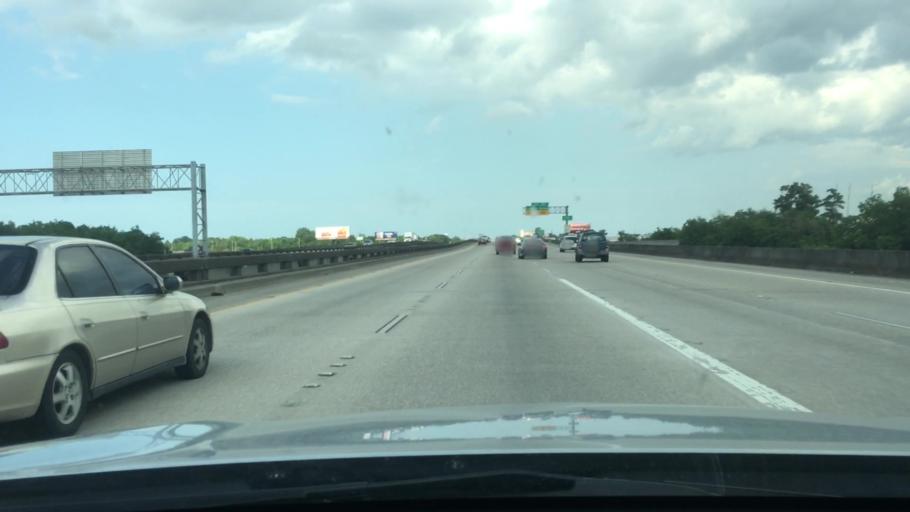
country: US
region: Louisiana
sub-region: Jefferson Parish
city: Kenner
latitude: 30.0059
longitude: -90.2826
